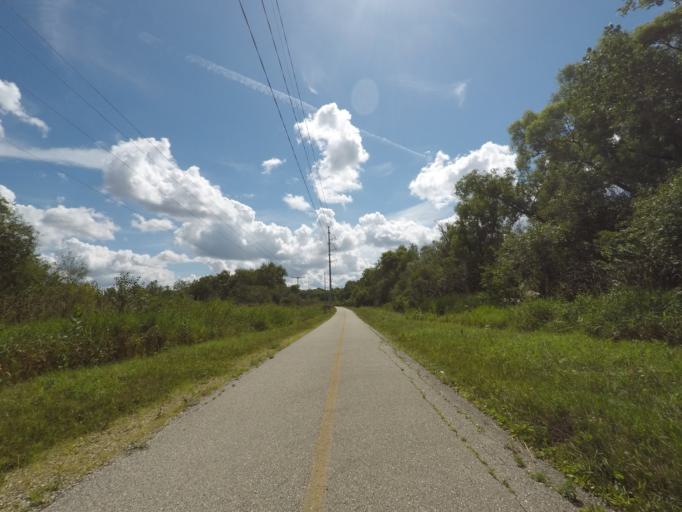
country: US
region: Wisconsin
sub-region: Waukesha County
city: Hartland
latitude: 43.0578
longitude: -88.3509
